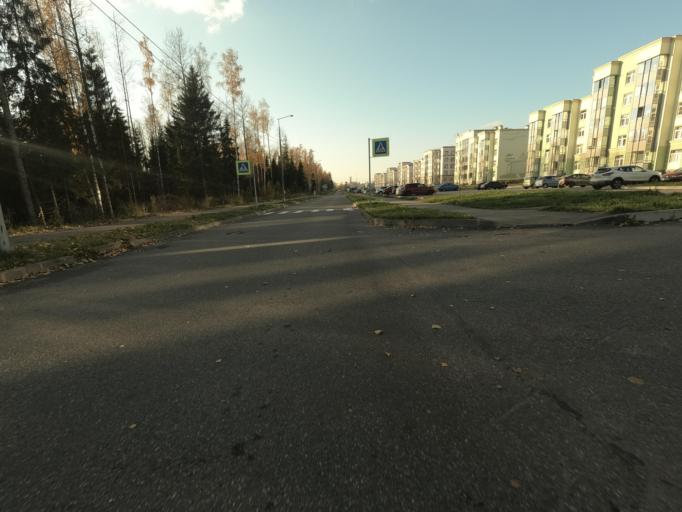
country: RU
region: Leningrad
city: Sertolovo
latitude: 60.1626
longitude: 30.1942
